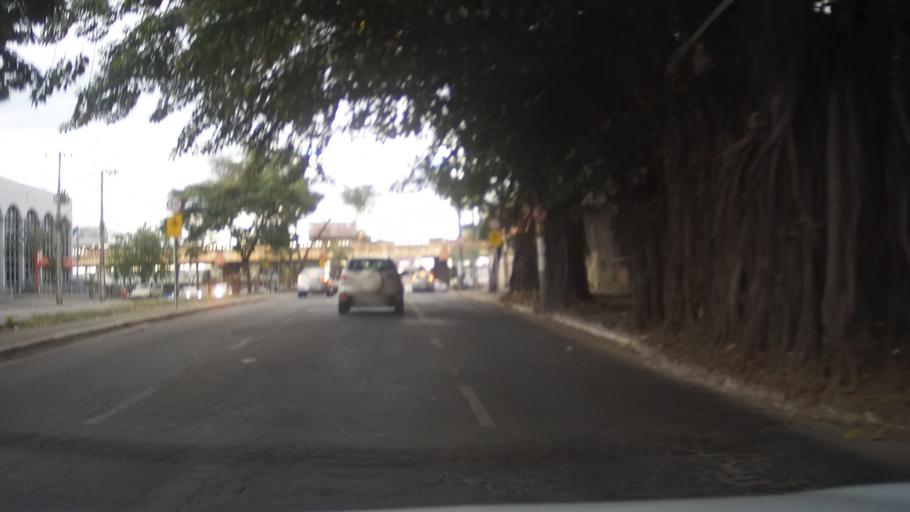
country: BR
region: Minas Gerais
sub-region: Contagem
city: Contagem
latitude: -19.9535
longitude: -44.0180
